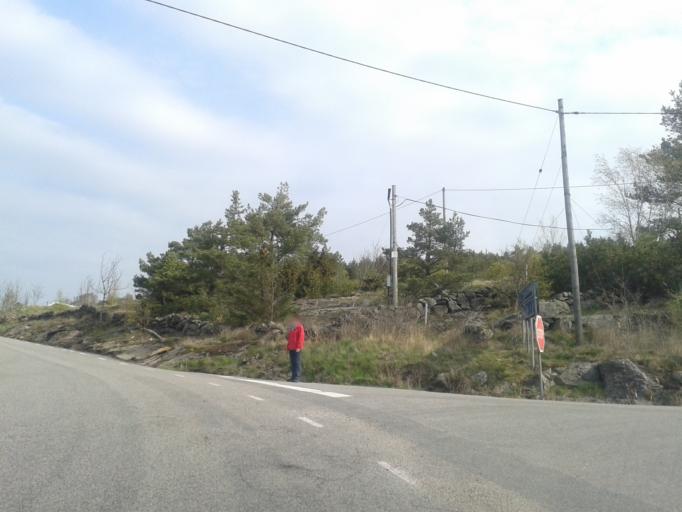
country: SE
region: Vaestra Goetaland
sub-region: Kungalvs Kommun
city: Kode
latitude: 57.9161
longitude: 11.8037
